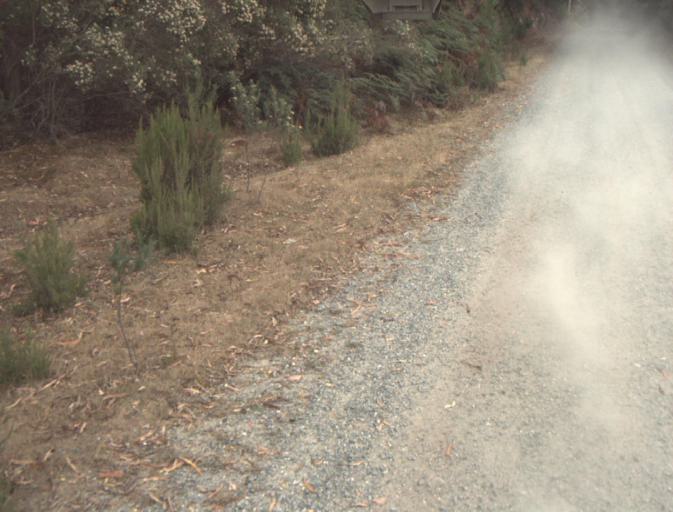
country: AU
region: Tasmania
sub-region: Launceston
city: Mayfield
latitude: -41.1534
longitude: 147.1727
